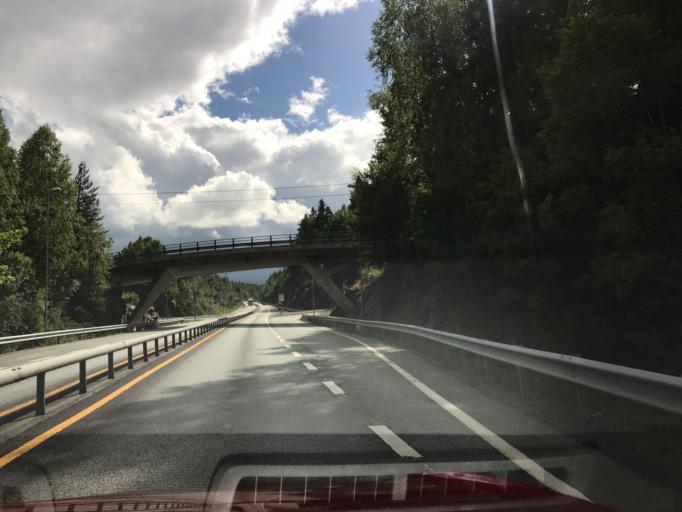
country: NO
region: Aust-Agder
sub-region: Gjerstad
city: Gjerstad
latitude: 58.8345
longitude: 9.0903
